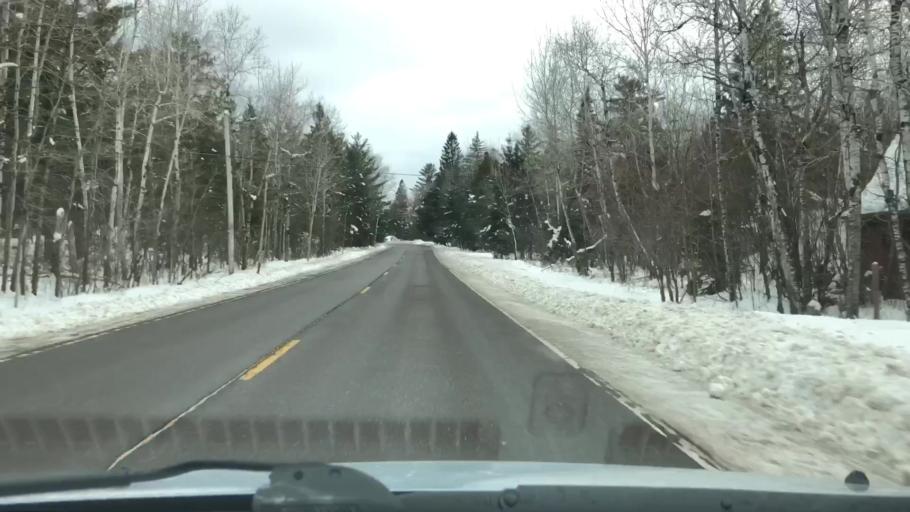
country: US
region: Minnesota
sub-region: Carlton County
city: Carlton
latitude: 46.6648
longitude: -92.4131
